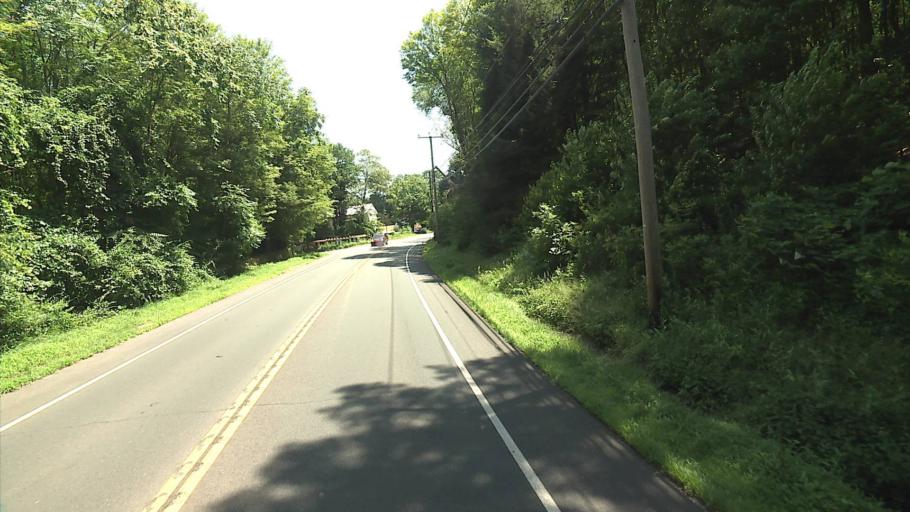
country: US
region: Connecticut
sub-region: Middlesex County
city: East Haddam
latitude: 41.4661
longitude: -72.4809
